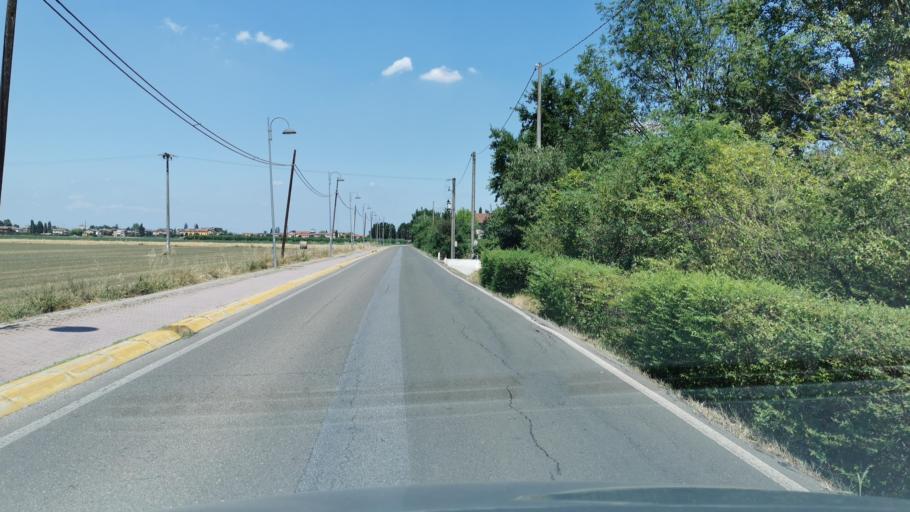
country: IT
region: Emilia-Romagna
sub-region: Provincia di Modena
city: Fossoli
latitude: 44.8081
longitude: 10.8885
